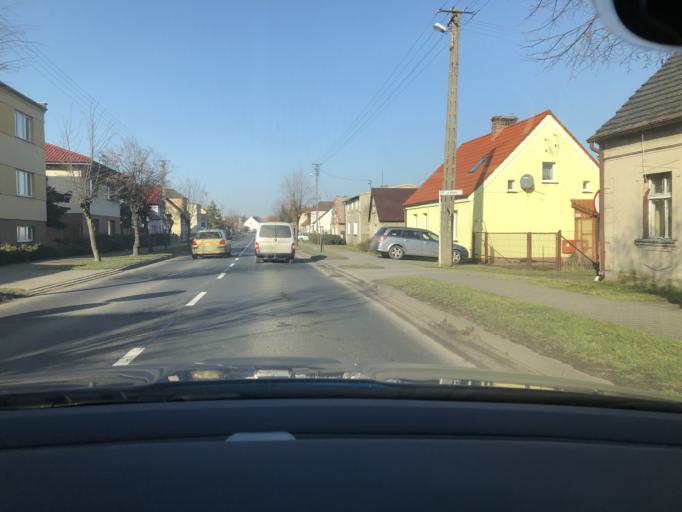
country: PL
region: Greater Poland Voivodeship
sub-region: Powiat szamotulski
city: Duszniki
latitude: 52.4428
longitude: 16.4090
